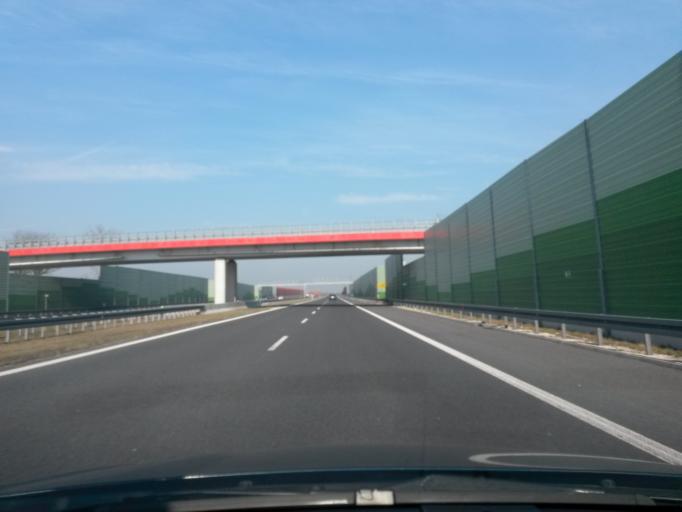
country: PL
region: Lodz Voivodeship
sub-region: Powiat leczycki
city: Piatek
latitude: 52.1260
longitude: 19.4951
